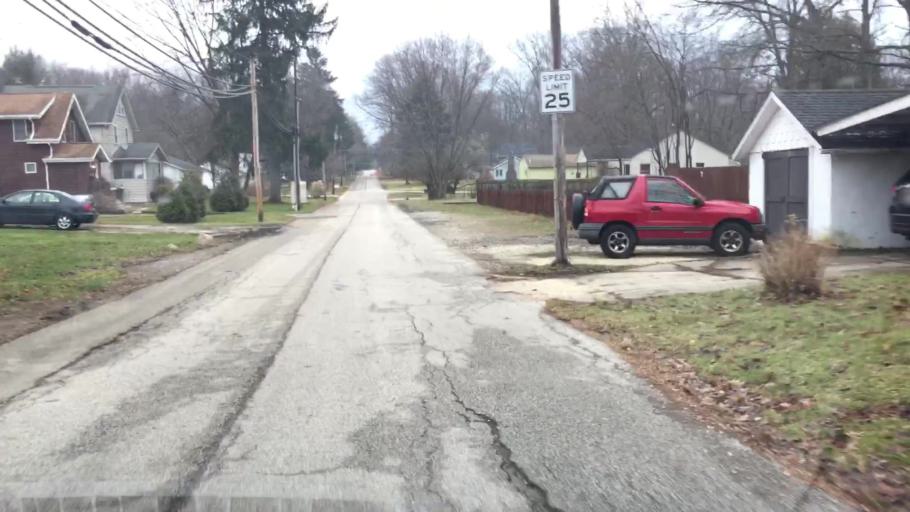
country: US
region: Ohio
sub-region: Summit County
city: Stow
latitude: 41.1631
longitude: -81.4379
